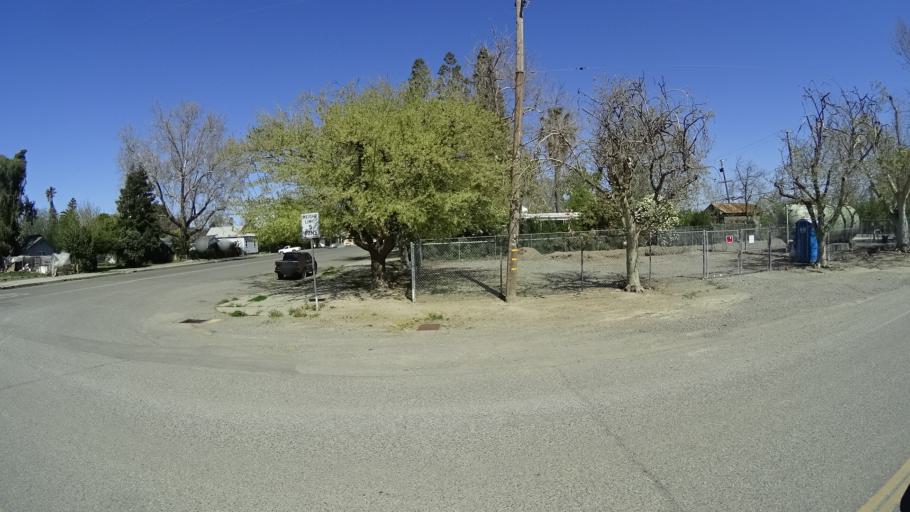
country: US
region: California
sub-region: Glenn County
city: Hamilton City
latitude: 39.7386
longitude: -122.0101
